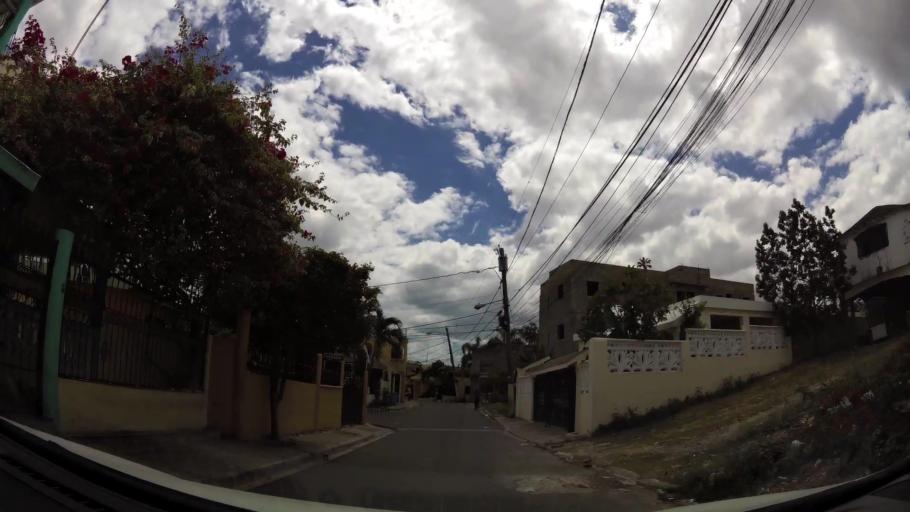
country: DO
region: Nacional
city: Ensanche Luperon
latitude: 18.5222
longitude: -69.9081
